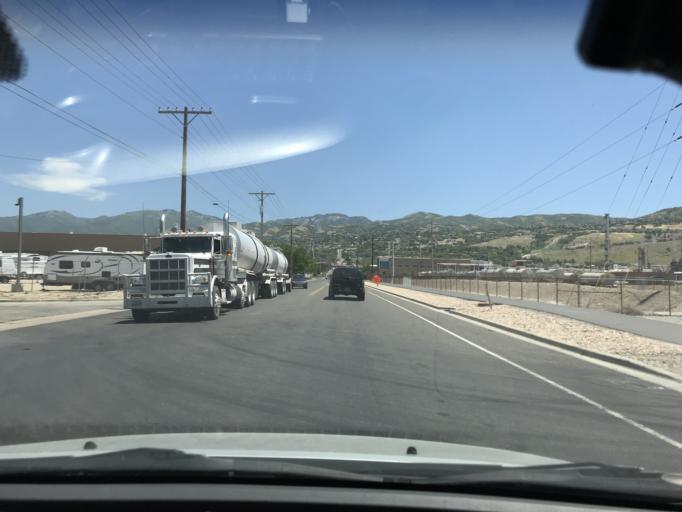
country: US
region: Utah
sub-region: Davis County
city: North Salt Lake
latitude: 40.8419
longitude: -111.9244
